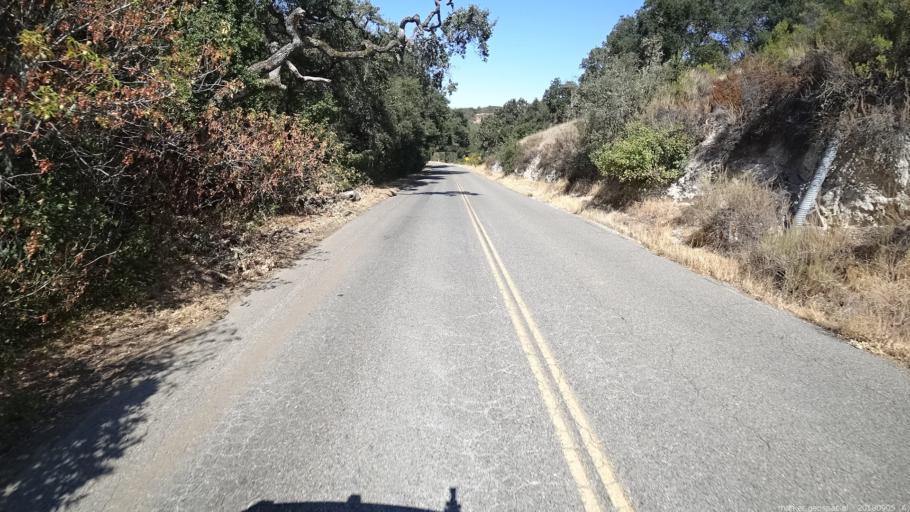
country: US
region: California
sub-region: Monterey County
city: Chualar
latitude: 36.4140
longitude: -121.5945
